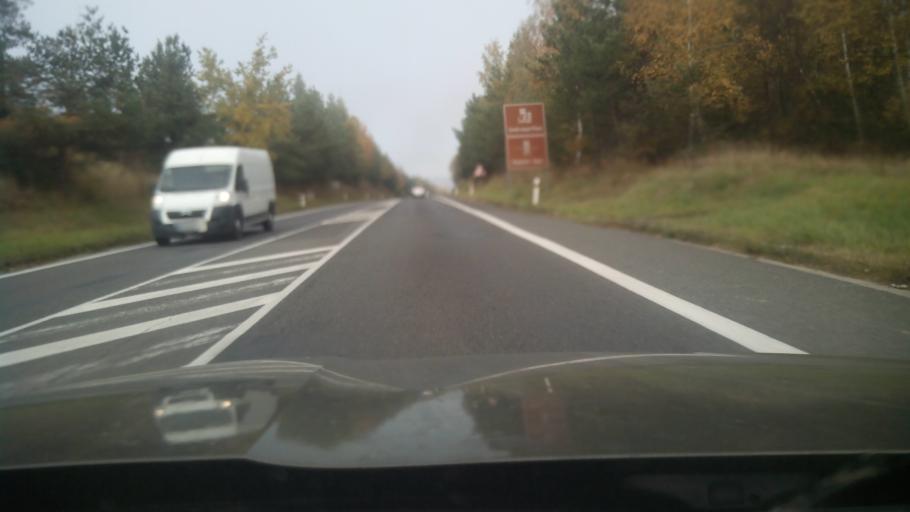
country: CZ
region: Central Bohemia
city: Milin
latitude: 49.6245
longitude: 14.0521
